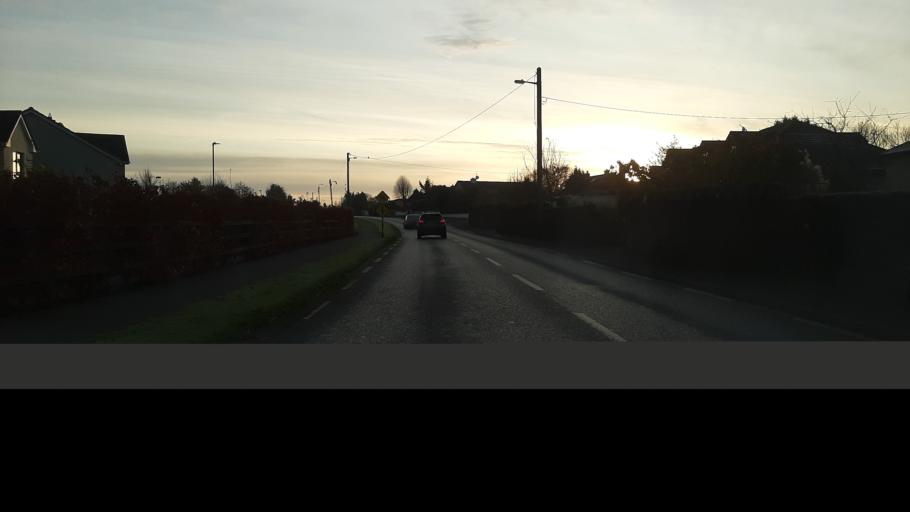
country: IE
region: Leinster
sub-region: Kildare
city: Rathangan
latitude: 53.2179
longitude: -6.9863
